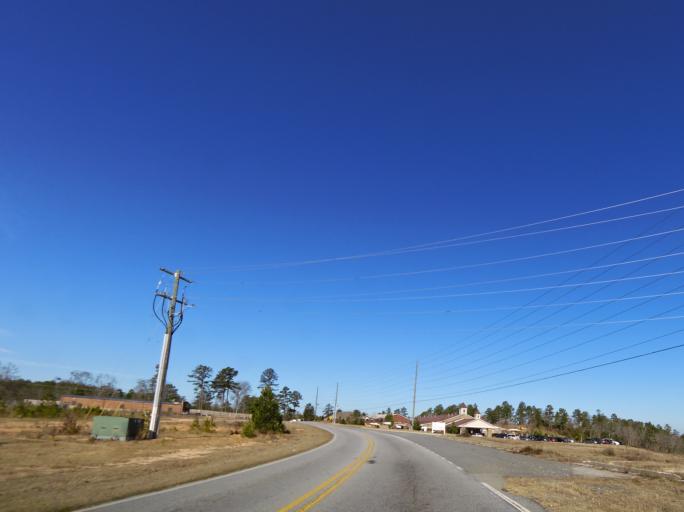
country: US
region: Georgia
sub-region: Bibb County
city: West Point
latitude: 32.7465
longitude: -83.7299
